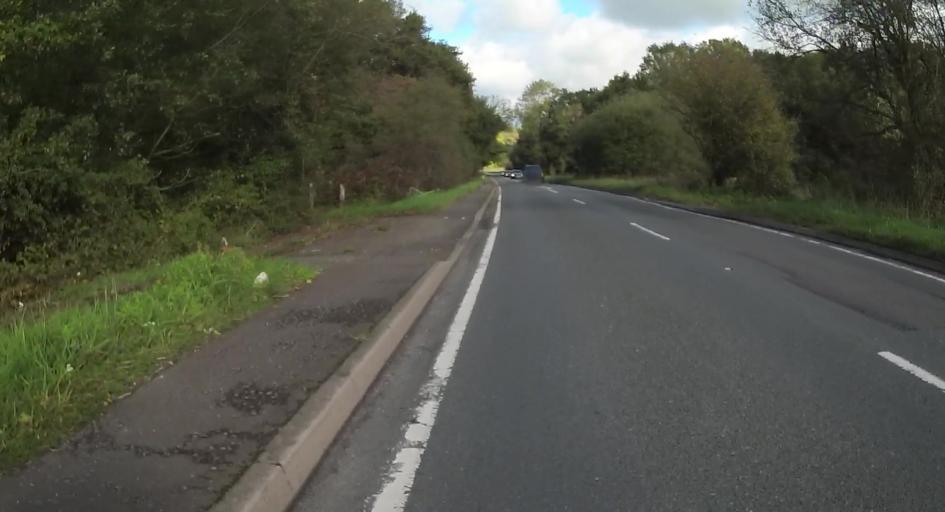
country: GB
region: England
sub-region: Hampshire
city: Odiham
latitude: 51.2624
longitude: -0.9291
